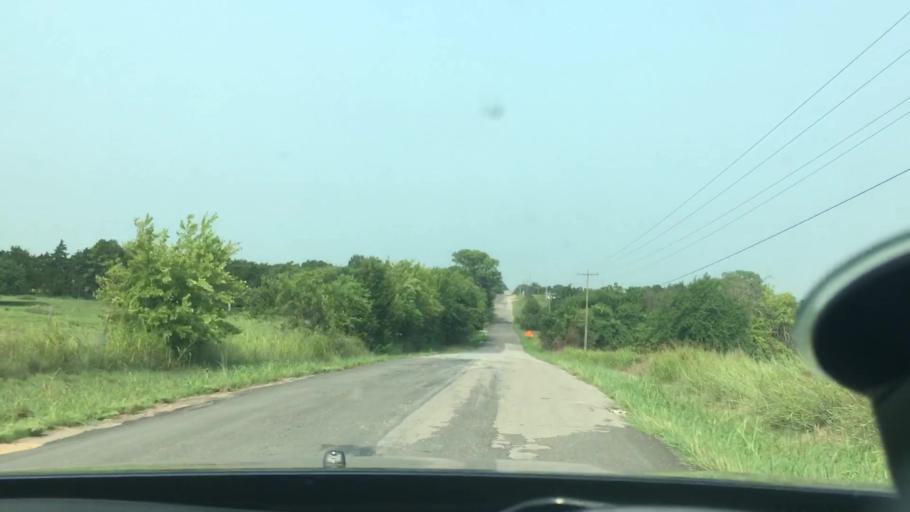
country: US
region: Oklahoma
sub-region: Garvin County
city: Lindsay
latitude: 34.8120
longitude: -97.6406
